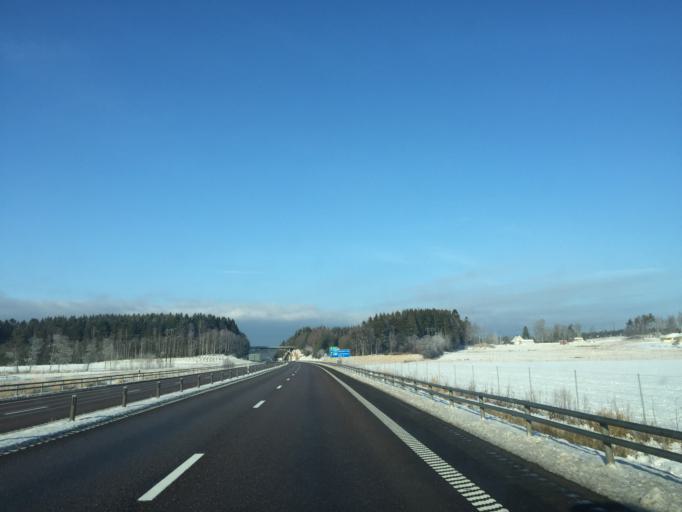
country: SE
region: Vaestra Goetaland
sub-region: Tanums Kommun
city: Tanumshede
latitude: 58.7280
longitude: 11.3429
